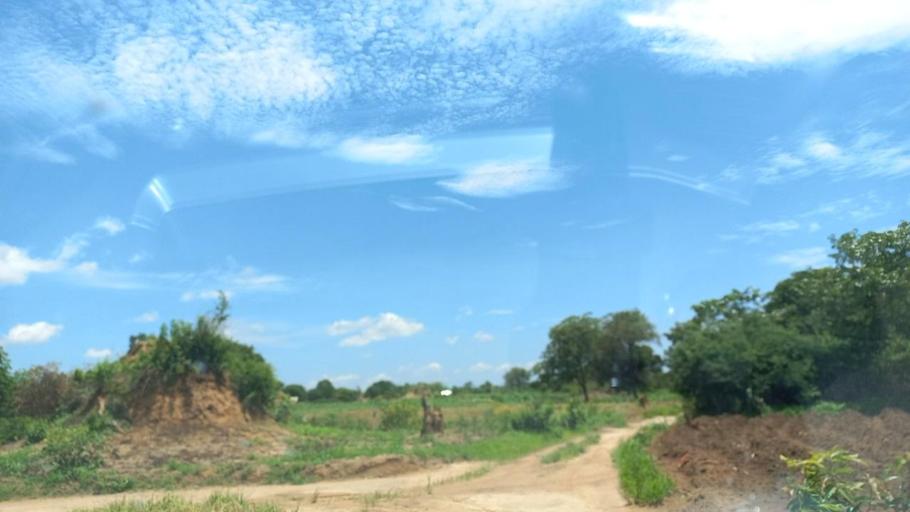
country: ZM
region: Copperbelt
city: Ndola
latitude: -12.8783
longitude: 28.4464
